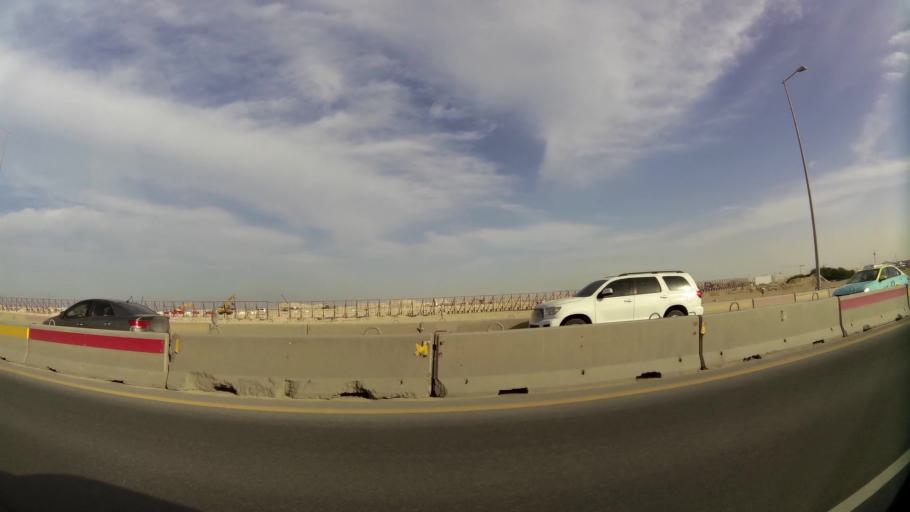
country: QA
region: Al Wakrah
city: Al Wakrah
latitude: 25.2251
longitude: 51.5907
